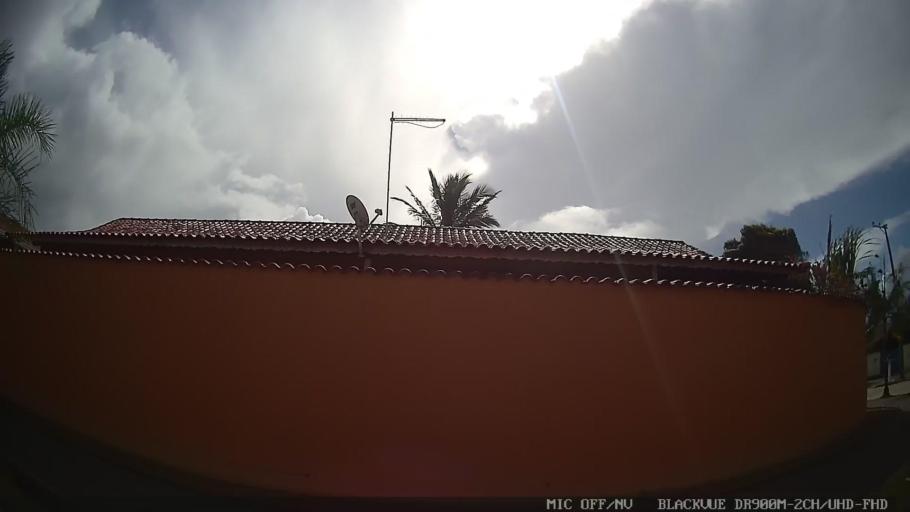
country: BR
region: Sao Paulo
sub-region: Itanhaem
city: Itanhaem
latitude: -24.2450
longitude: -46.8932
